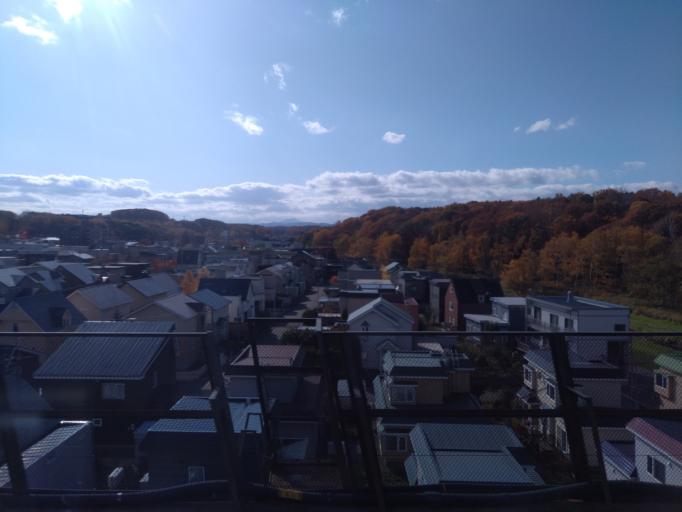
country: JP
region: Hokkaido
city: Kitahiroshima
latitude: 42.9873
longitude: 141.5606
